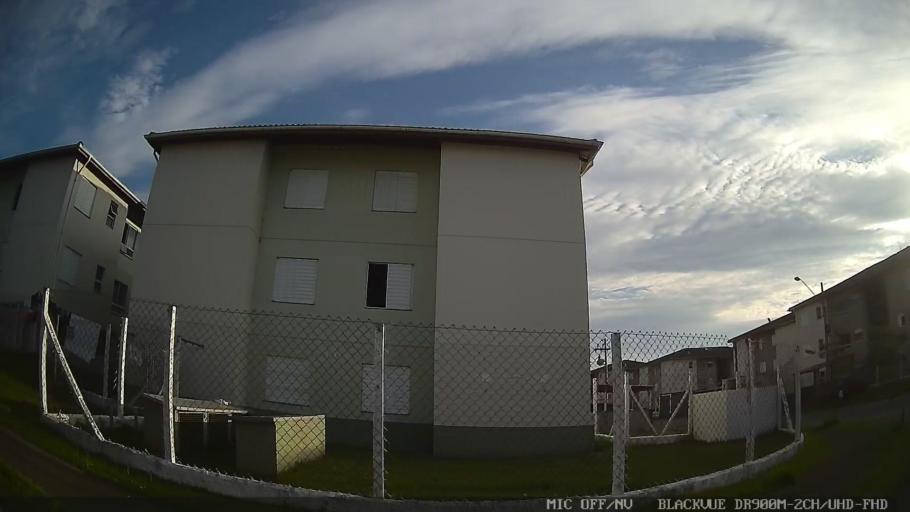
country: BR
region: Sao Paulo
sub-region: Itanhaem
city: Itanhaem
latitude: -24.1506
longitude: -46.7947
